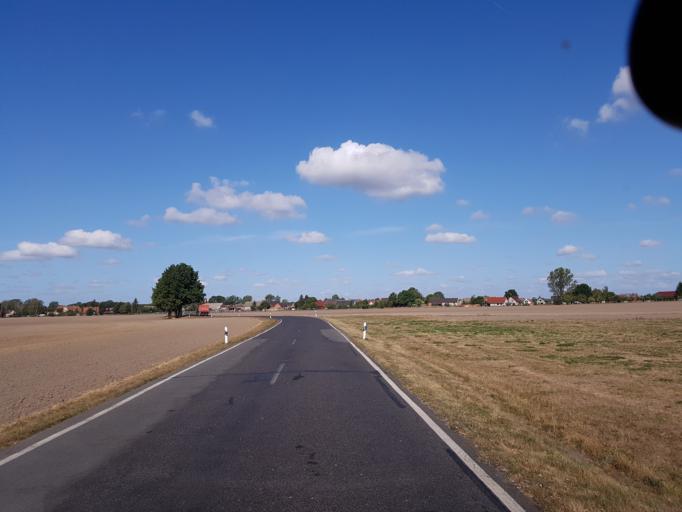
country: DE
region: Brandenburg
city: Sonnewalde
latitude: 51.7078
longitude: 13.6415
